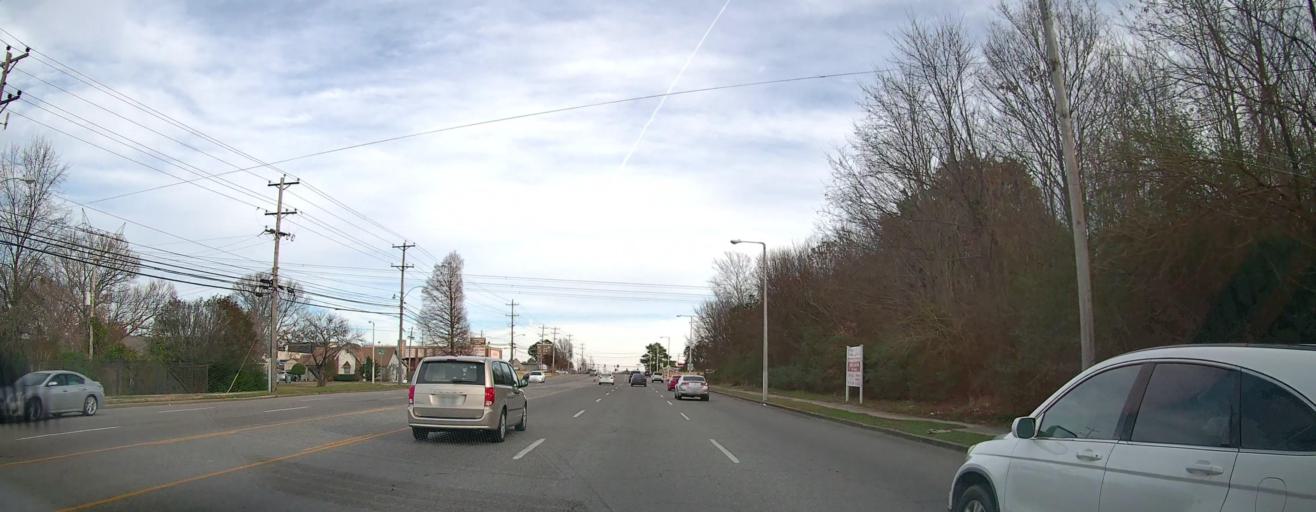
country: US
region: Tennessee
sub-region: Shelby County
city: Germantown
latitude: 35.0492
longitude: -89.8345
